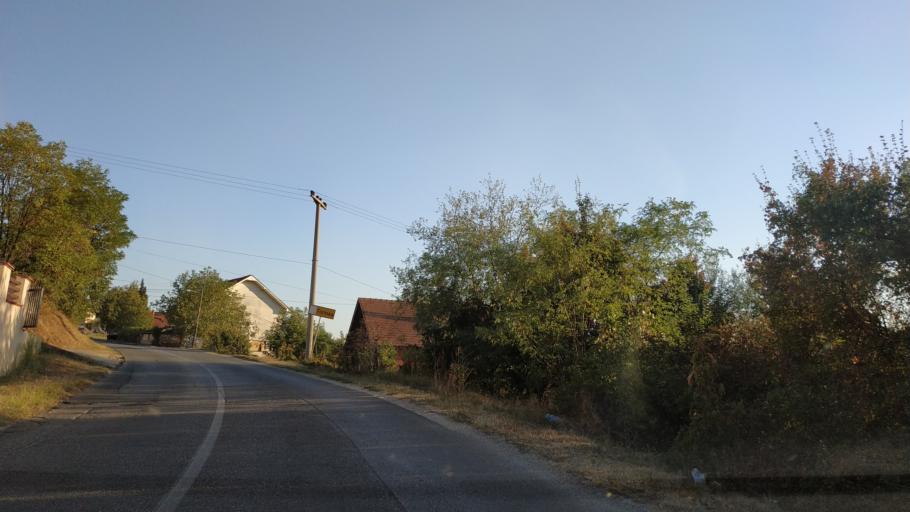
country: RS
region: Central Serbia
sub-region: Sumadijski Okrug
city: Topola
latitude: 44.2587
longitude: 20.6719
